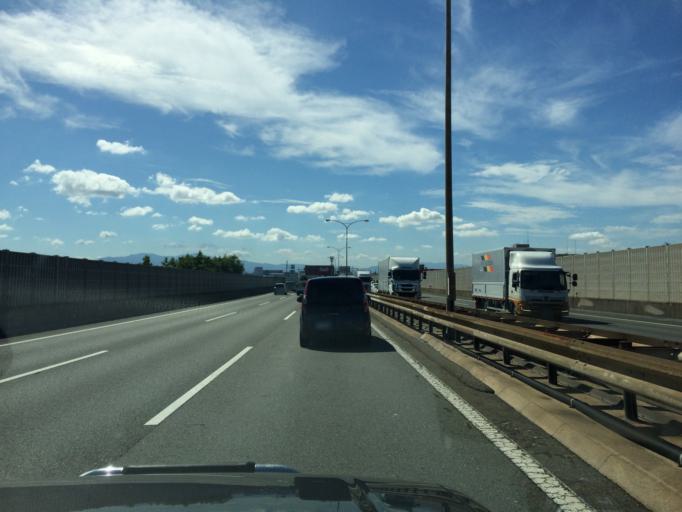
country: JP
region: Osaka
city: Yao
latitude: 34.6598
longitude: 135.5984
